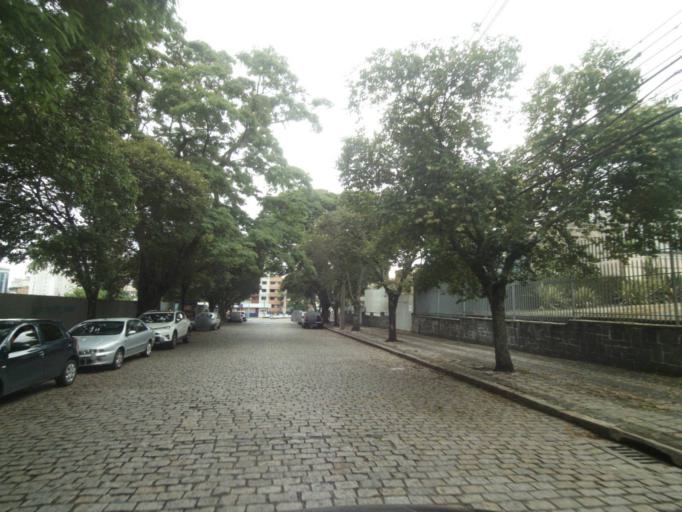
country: BR
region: Parana
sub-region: Curitiba
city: Curitiba
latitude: -25.4161
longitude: -49.2638
